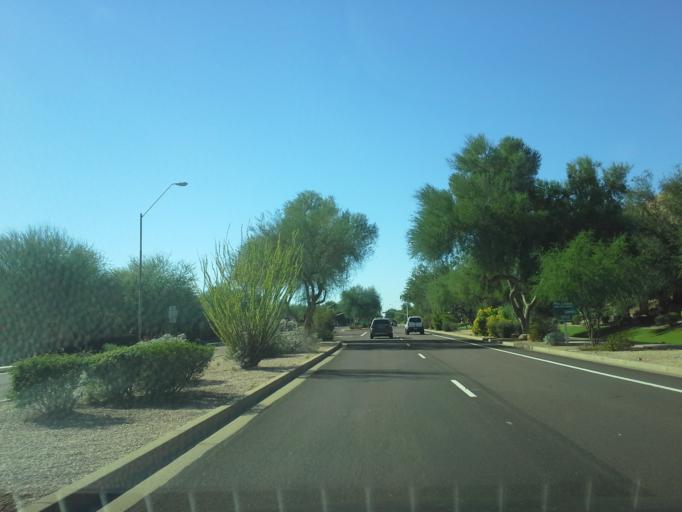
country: US
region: Arizona
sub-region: Maricopa County
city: Paradise Valley
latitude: 33.6401
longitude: -111.8933
